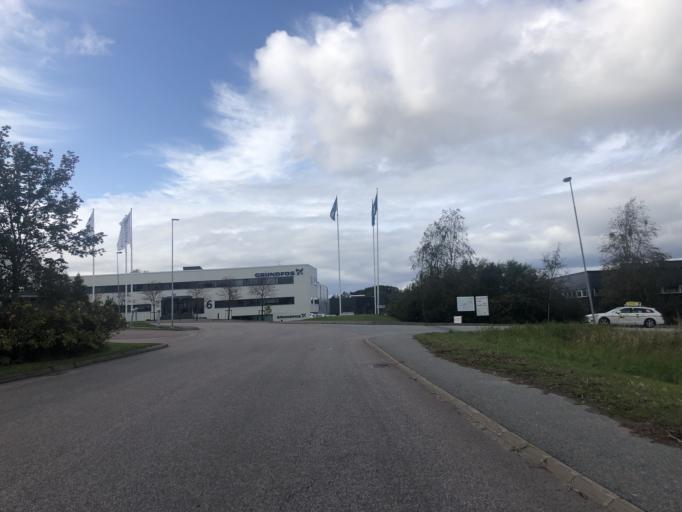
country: SE
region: Vaestra Goetaland
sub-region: Molndal
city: Moelndal
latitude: 57.6427
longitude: 11.9858
